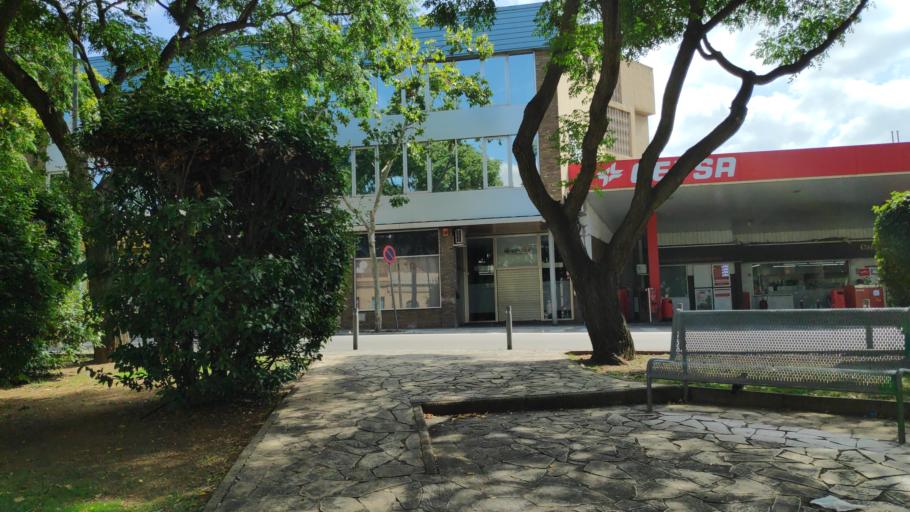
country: ES
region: Catalonia
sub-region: Provincia de Barcelona
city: Sabadell
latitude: 41.5393
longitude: 2.0995
